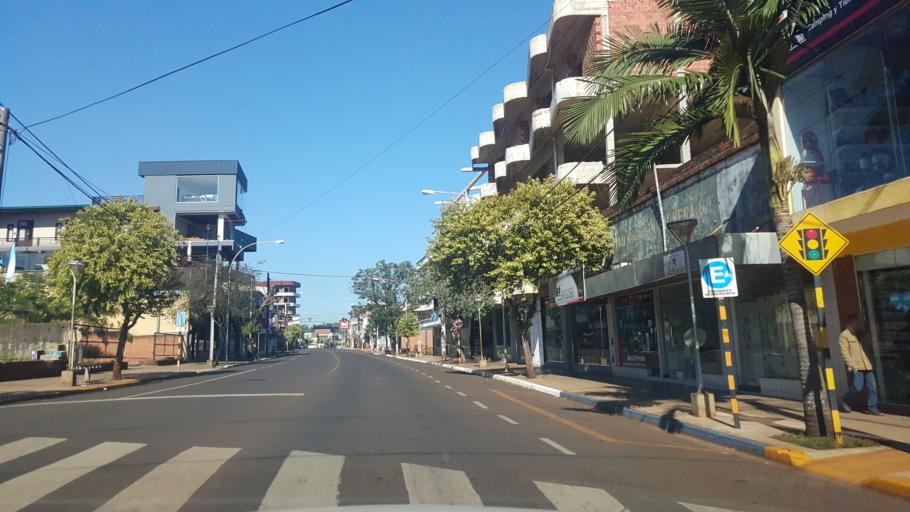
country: AR
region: Misiones
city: Puerto Rico
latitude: -26.8097
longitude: -55.0260
